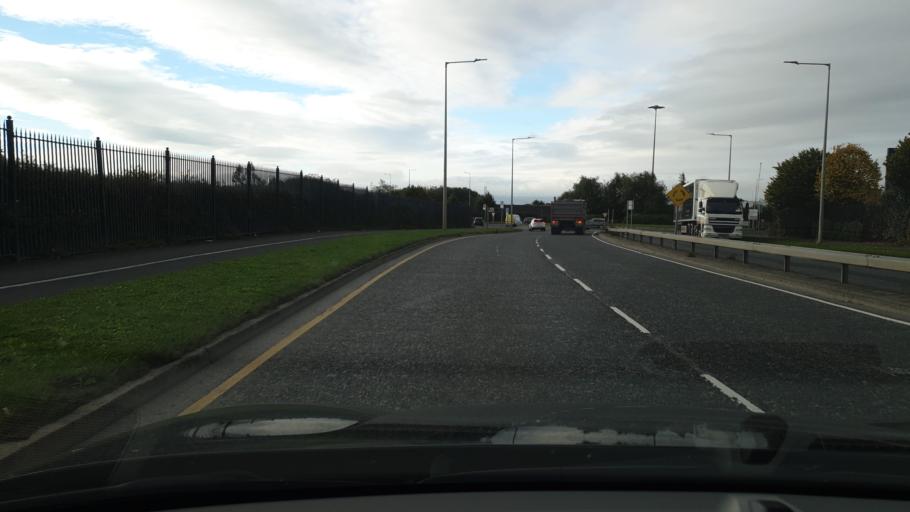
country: IE
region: Leinster
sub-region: Fingal County
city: Blanchardstown
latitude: 53.4096
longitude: -6.3685
